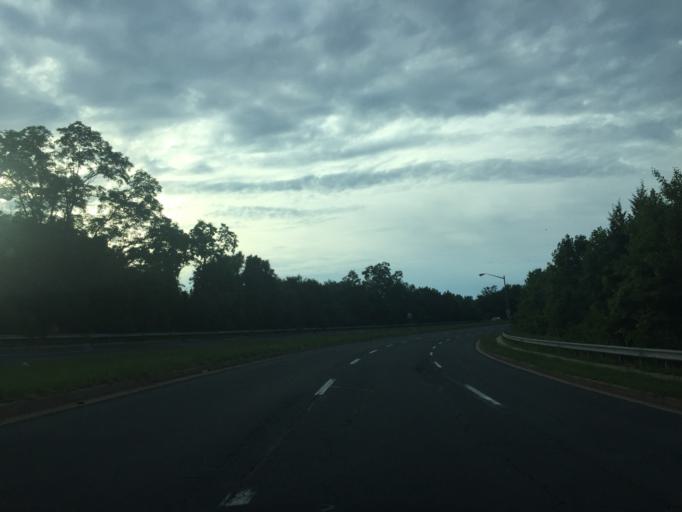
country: US
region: Maryland
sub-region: Baltimore County
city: Rossville
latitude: 39.3405
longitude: -76.4865
